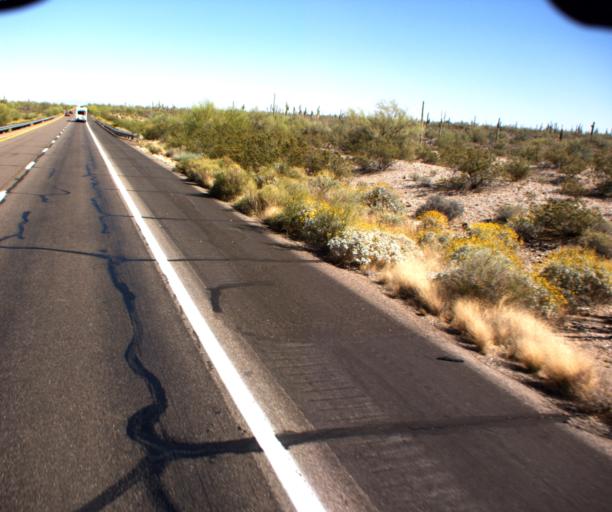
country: US
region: Arizona
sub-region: Pinal County
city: Maricopa
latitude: 32.8322
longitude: -112.0793
